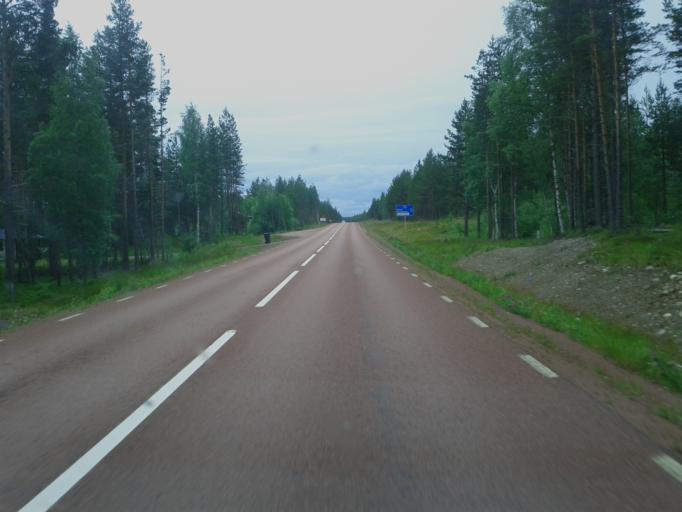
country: NO
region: Hedmark
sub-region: Trysil
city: Innbygda
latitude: 61.6854
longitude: 13.1638
